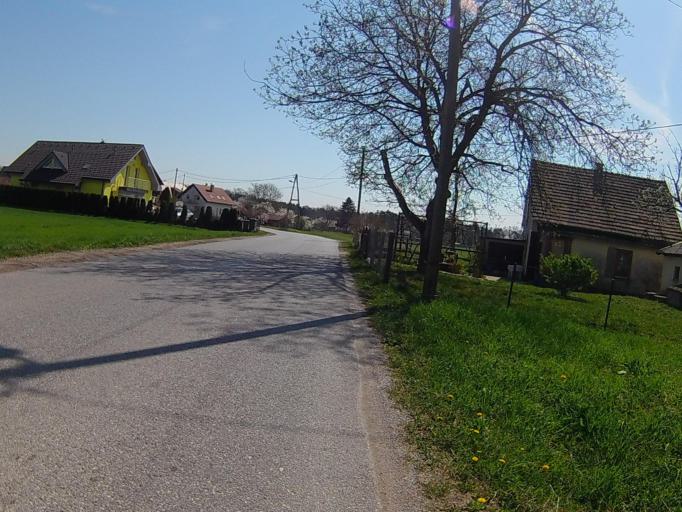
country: SI
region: Hoce-Slivnica
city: Rogoza
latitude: 46.4978
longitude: 15.6825
